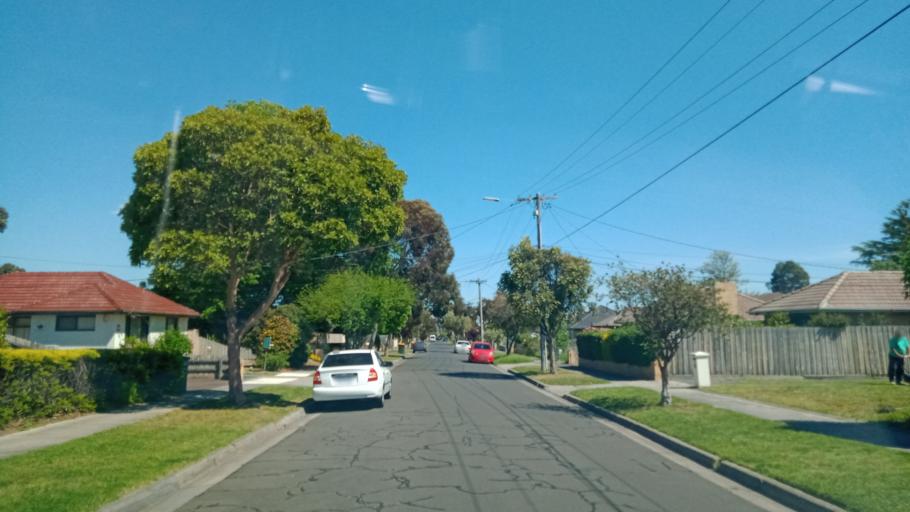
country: AU
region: Victoria
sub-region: Greater Dandenong
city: Springvale
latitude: -37.9293
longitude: 145.1644
